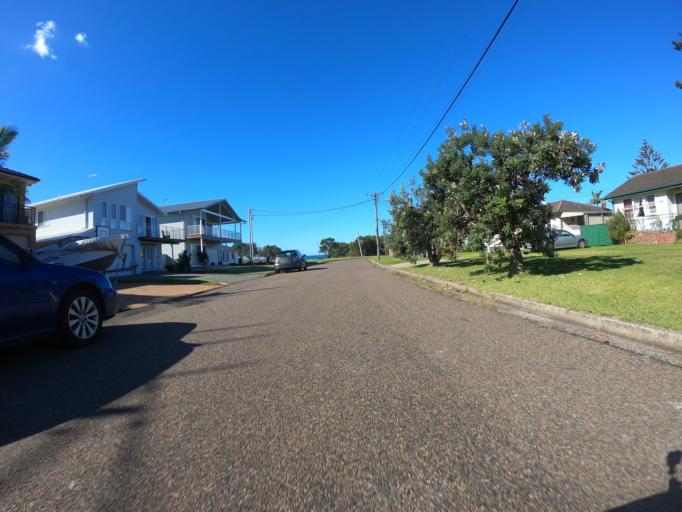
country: AU
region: New South Wales
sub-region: Wollongong
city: Bulli
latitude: -34.3548
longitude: 150.9171
